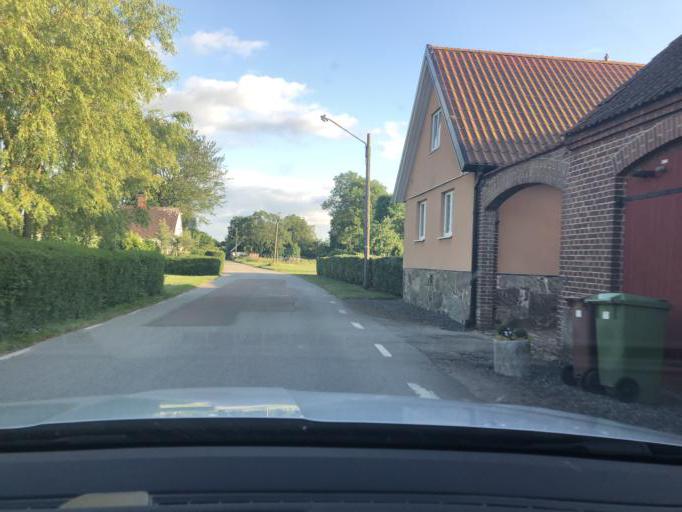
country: SE
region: Skane
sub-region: Simrishamns Kommun
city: Simrishamn
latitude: 55.4988
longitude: 14.2032
